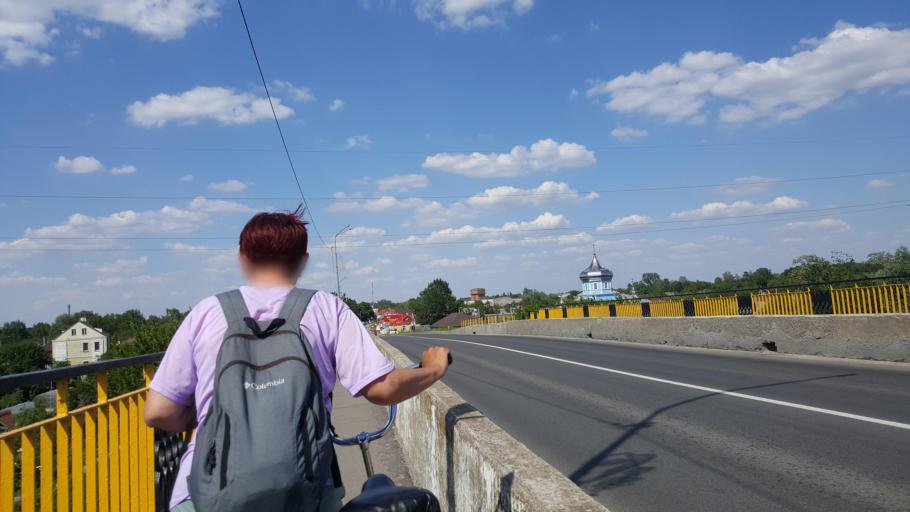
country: BY
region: Brest
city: Kobryn
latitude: 52.2156
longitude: 24.3591
